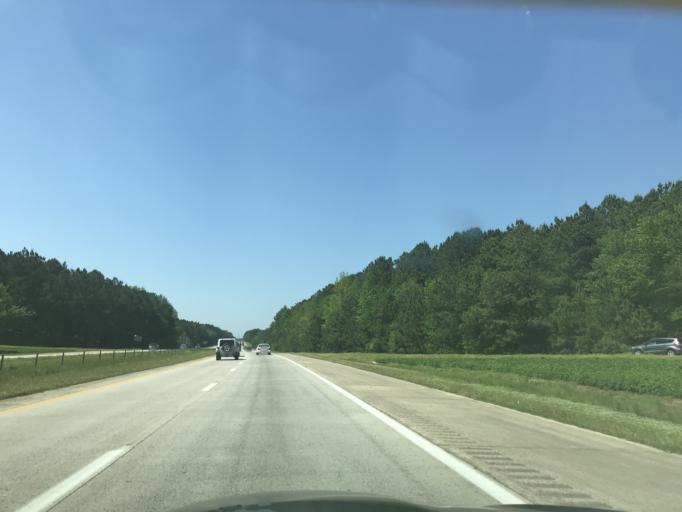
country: US
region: North Carolina
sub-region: Johnston County
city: Benson
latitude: 35.5176
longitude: -78.5582
